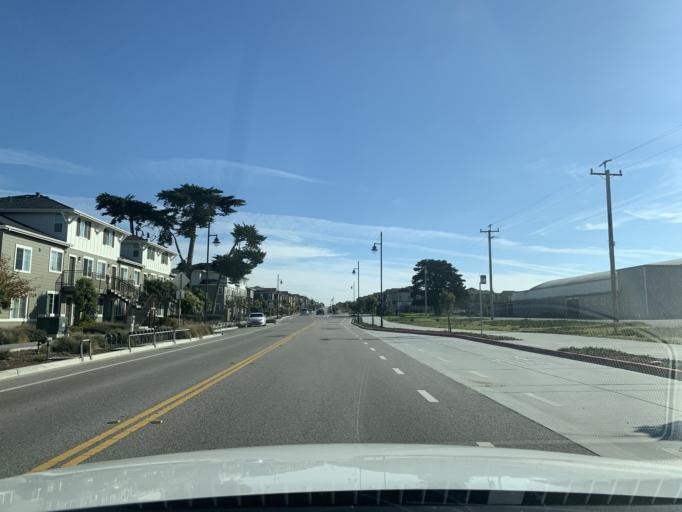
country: US
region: California
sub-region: Monterey County
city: Marina
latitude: 36.6625
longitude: -121.8109
